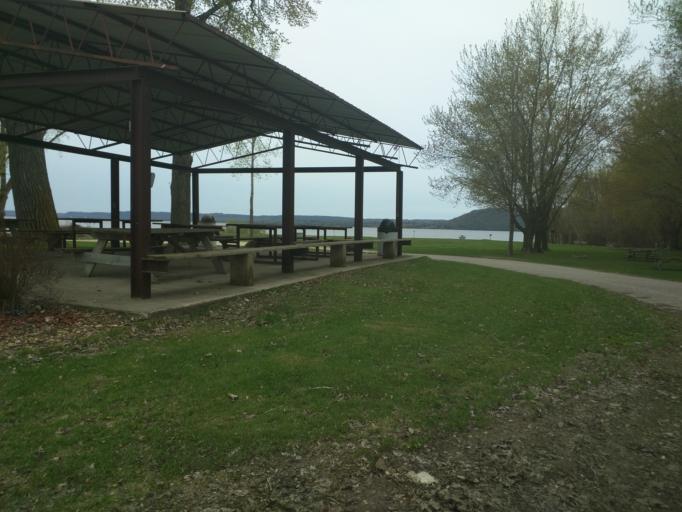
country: US
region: Minnesota
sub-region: Wabasha County
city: Lake City
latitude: 44.5600
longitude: -92.3102
